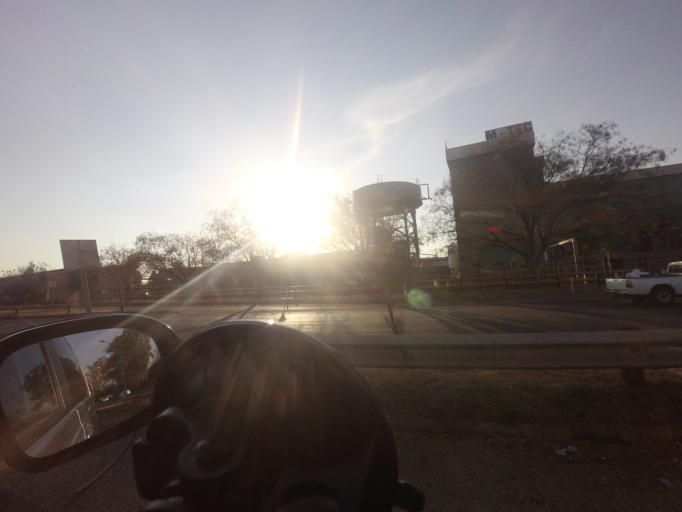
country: ZA
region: Gauteng
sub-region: Sedibeng District Municipality
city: Vereeniging
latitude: -26.6620
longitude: 27.9445
